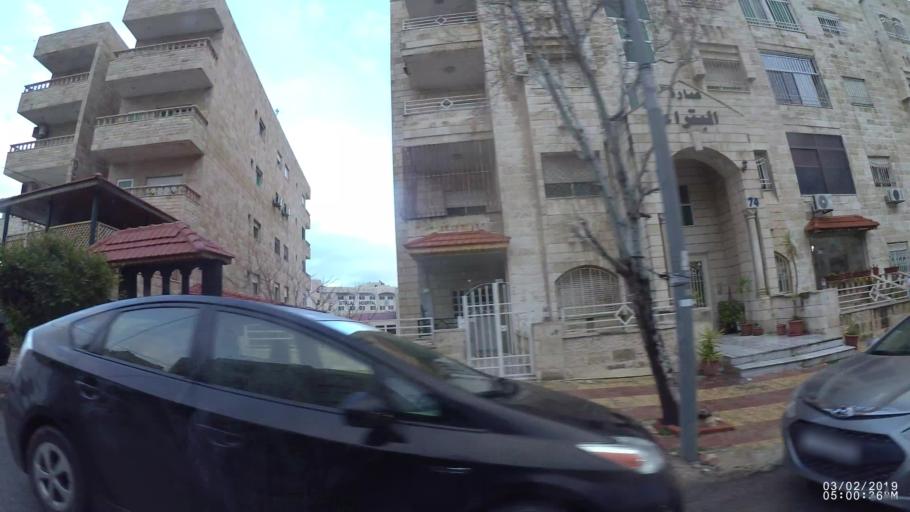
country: JO
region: Amman
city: Amman
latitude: 31.9797
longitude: 35.9144
